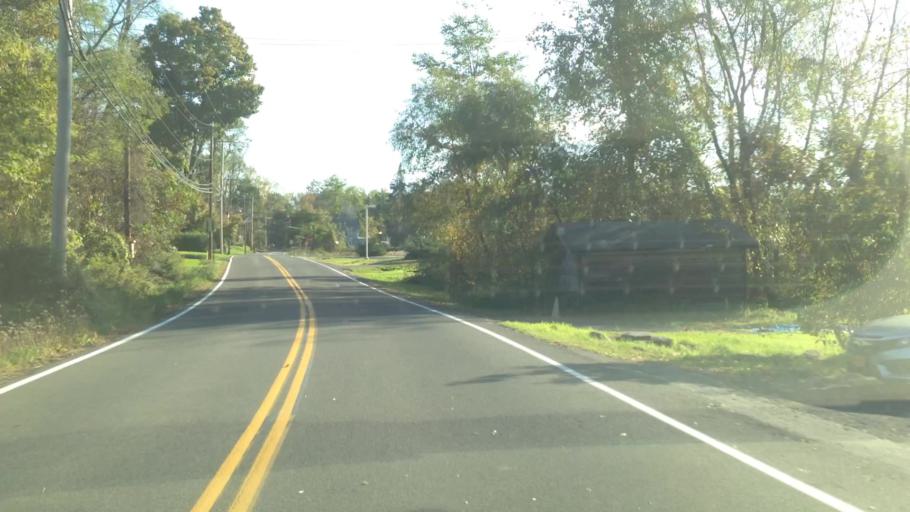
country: US
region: New York
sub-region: Dutchess County
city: Hyde Park
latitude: 41.8266
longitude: -73.9684
